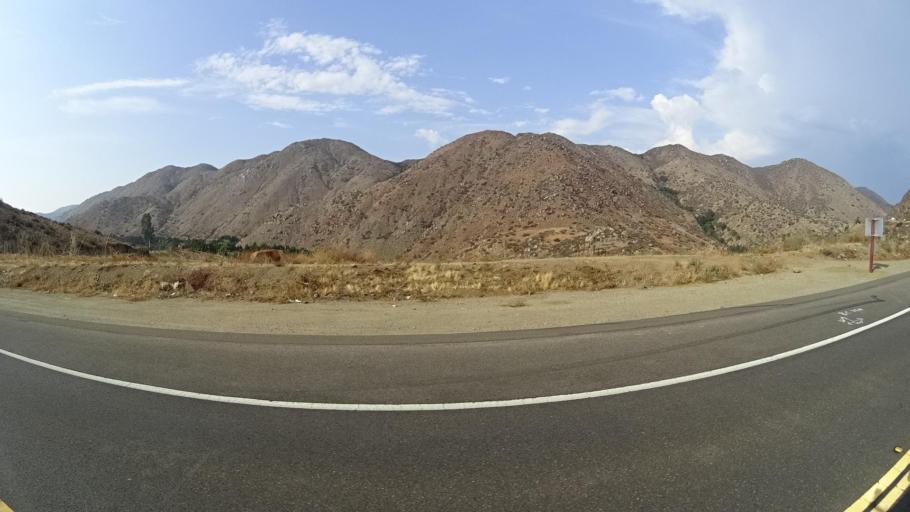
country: US
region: California
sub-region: San Diego County
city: San Pasqual
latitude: 33.0828
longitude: -116.9199
